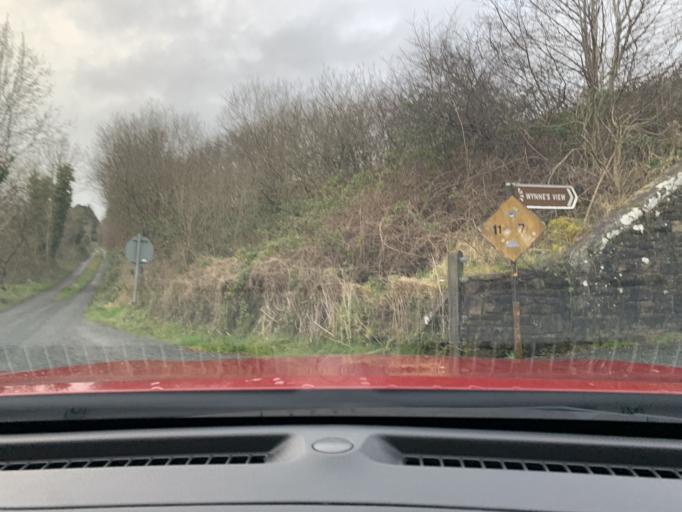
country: IE
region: Connaught
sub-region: Roscommon
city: Boyle
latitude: 53.9793
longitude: -8.4175
